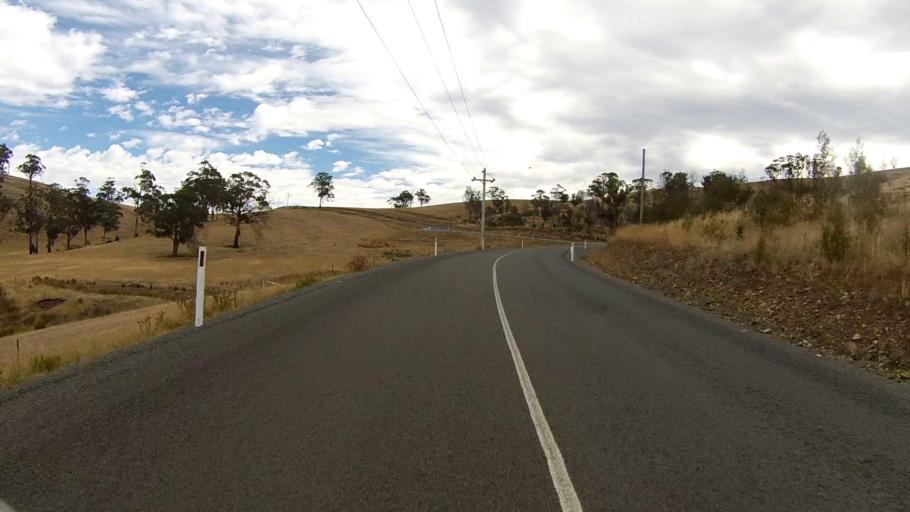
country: AU
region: Tasmania
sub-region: Sorell
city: Sorell
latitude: -42.8838
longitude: 147.7190
